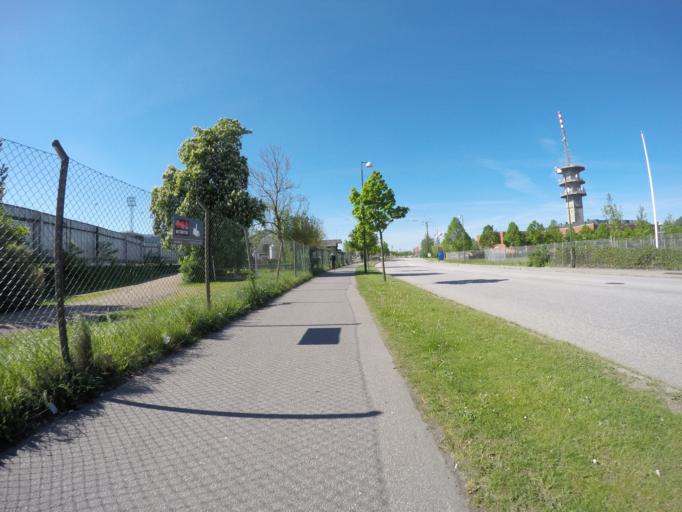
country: SE
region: Skane
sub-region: Malmo
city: Oxie
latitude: 55.5742
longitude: 13.0603
